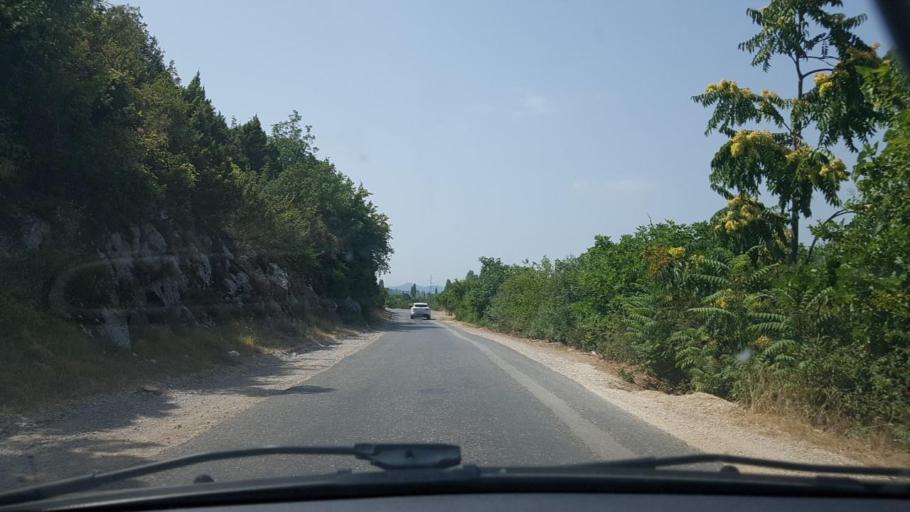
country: BA
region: Federation of Bosnia and Herzegovina
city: Tasovcici
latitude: 43.0328
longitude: 17.7376
